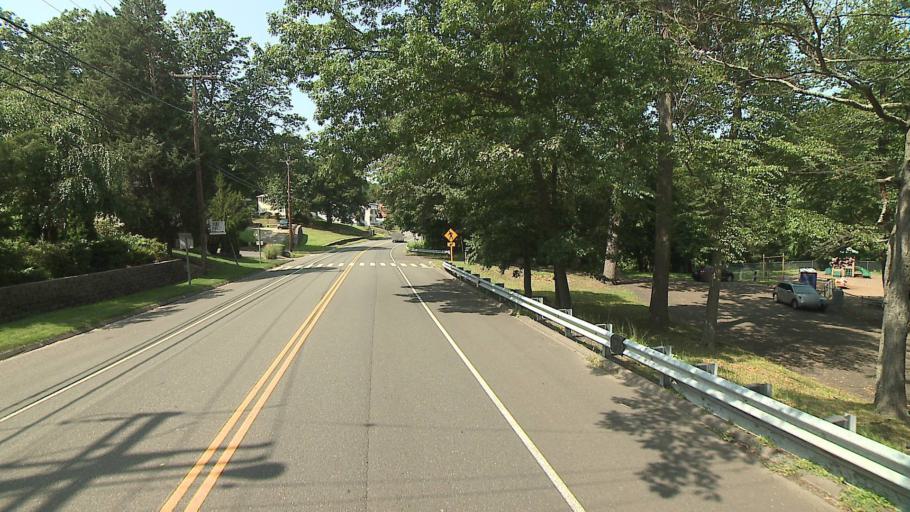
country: US
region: Connecticut
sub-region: Fairfield County
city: Shelton
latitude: 41.3248
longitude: -73.1064
